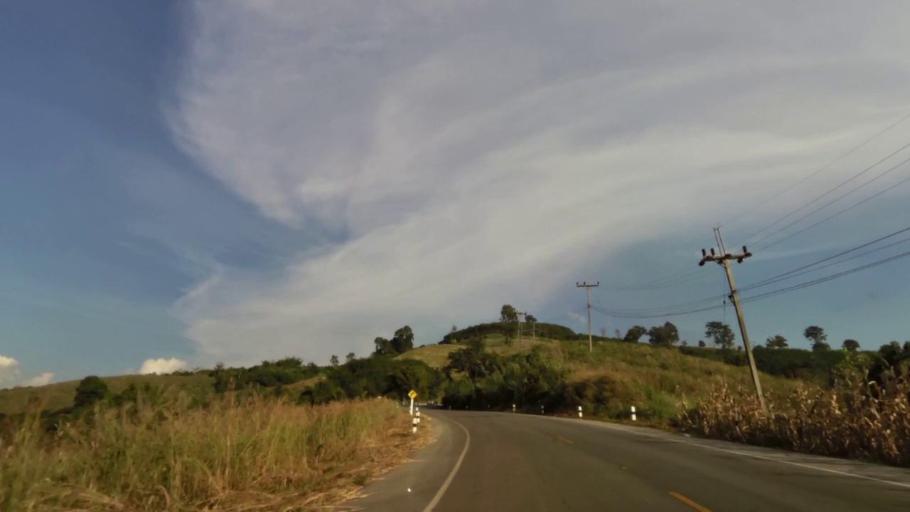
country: TH
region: Chiang Rai
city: Khun Tan
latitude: 19.8663
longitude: 100.4159
